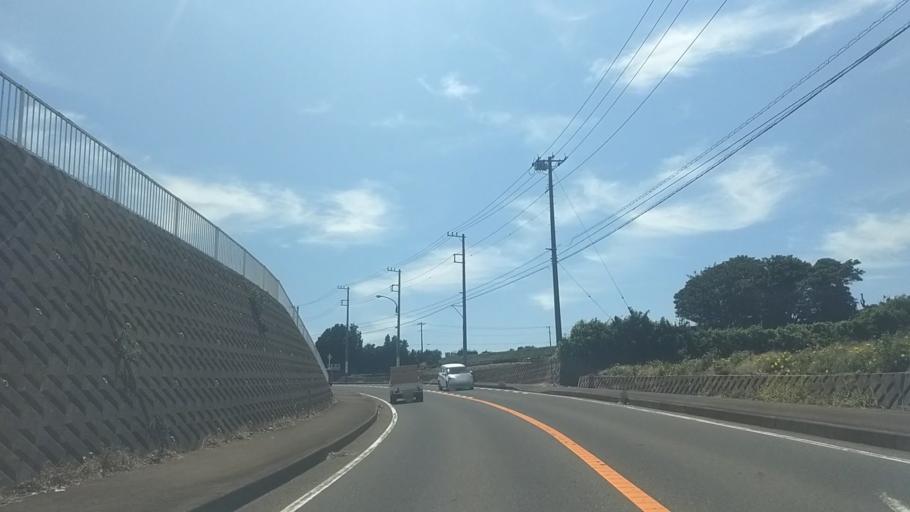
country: JP
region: Kanagawa
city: Miura
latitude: 35.1549
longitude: 139.6701
